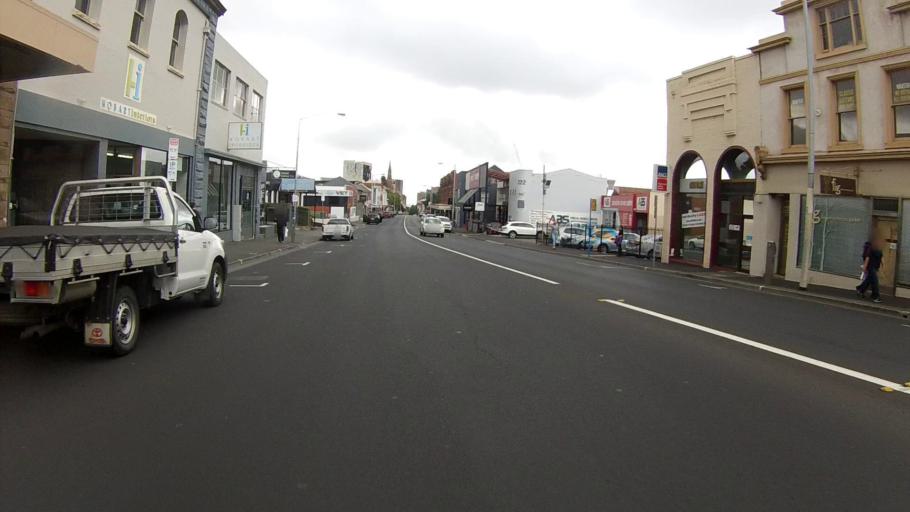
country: AU
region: Tasmania
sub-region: Hobart
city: Hobart
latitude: -42.8779
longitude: 147.3197
